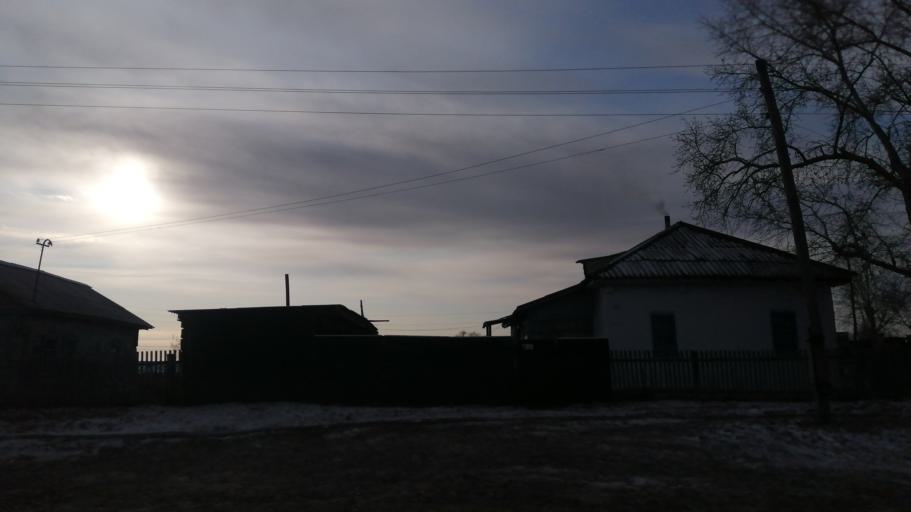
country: RU
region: Novosibirsk
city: Krasnozerskoye
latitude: 53.9866
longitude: 78.7125
